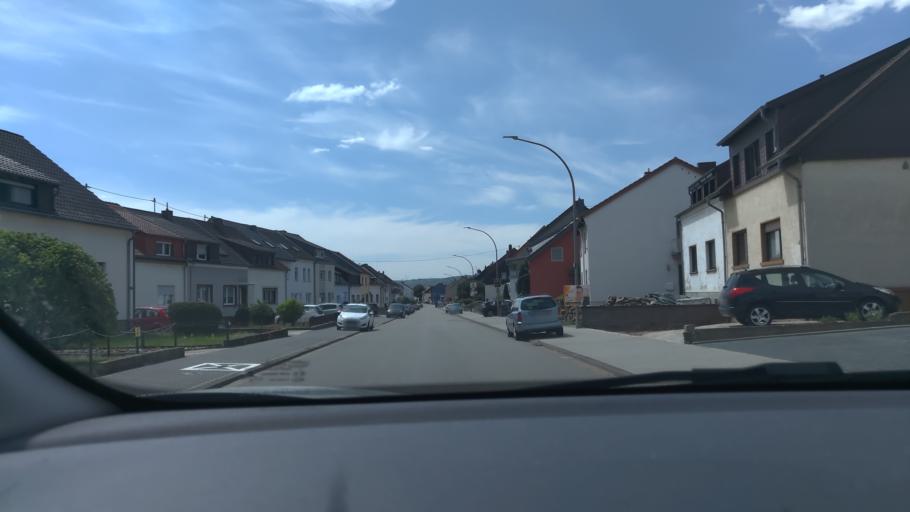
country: DE
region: Saarland
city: Saarlouis
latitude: 49.3380
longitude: 6.7621
